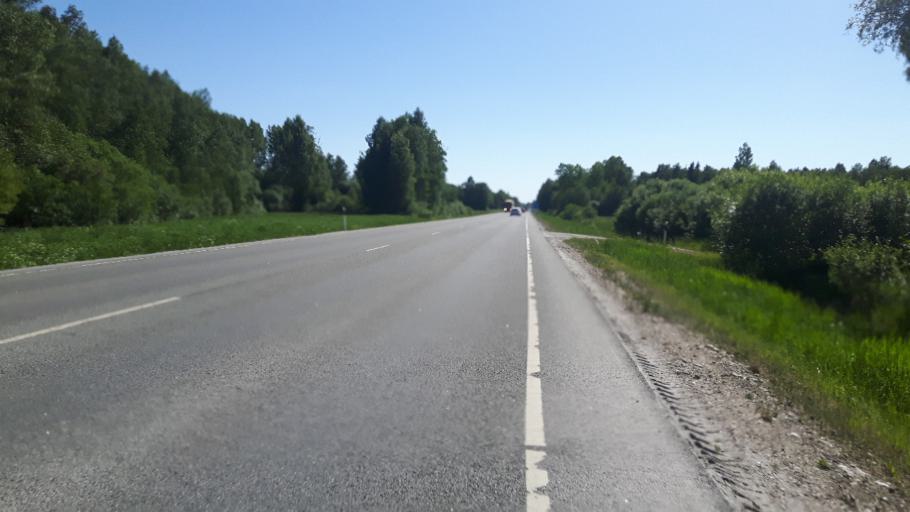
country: EE
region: Raplamaa
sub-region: Rapla vald
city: Rapla
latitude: 59.0210
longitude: 24.8090
